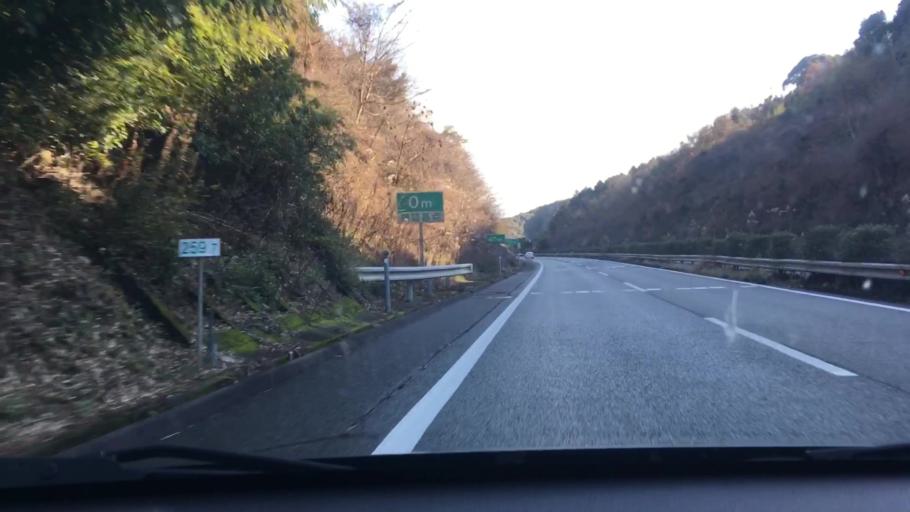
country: JP
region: Kumamoto
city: Hitoyoshi
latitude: 32.1740
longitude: 130.7900
